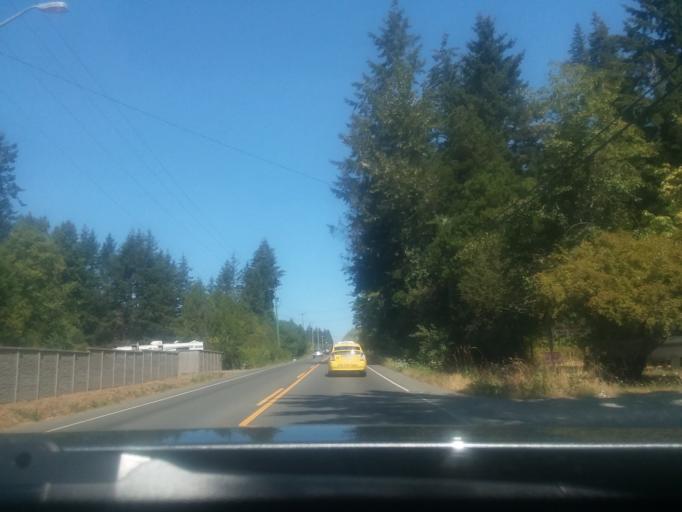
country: CA
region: British Columbia
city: Courtenay
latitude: 49.6954
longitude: -124.9346
